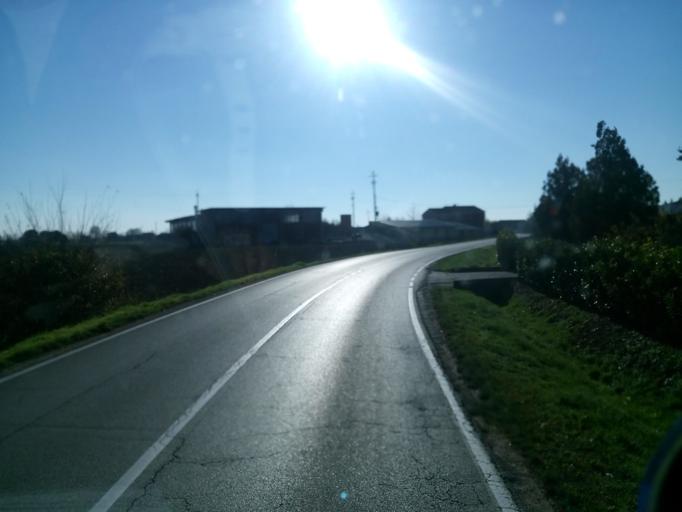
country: IT
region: Veneto
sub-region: Provincia di Vicenza
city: Sossano
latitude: 45.3684
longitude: 11.5211
